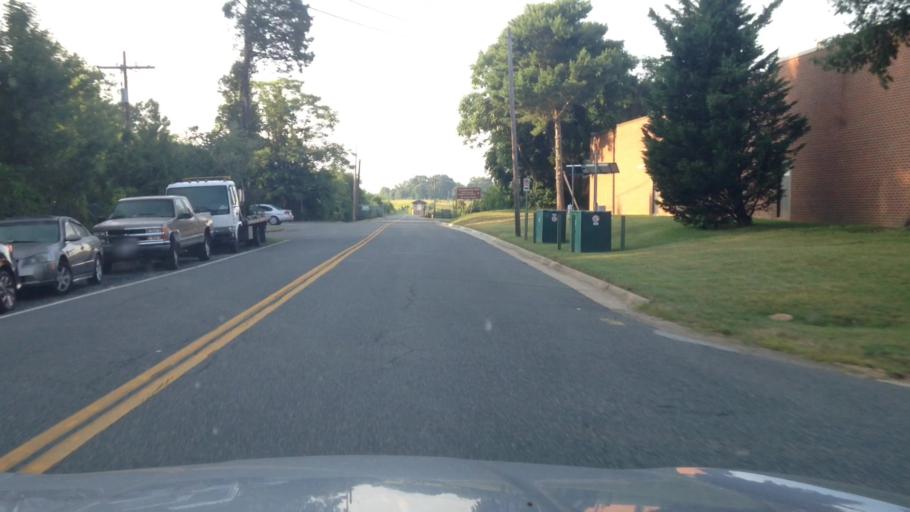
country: US
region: Virginia
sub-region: Prince William County
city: Woodbridge
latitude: 38.6503
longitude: -77.2444
